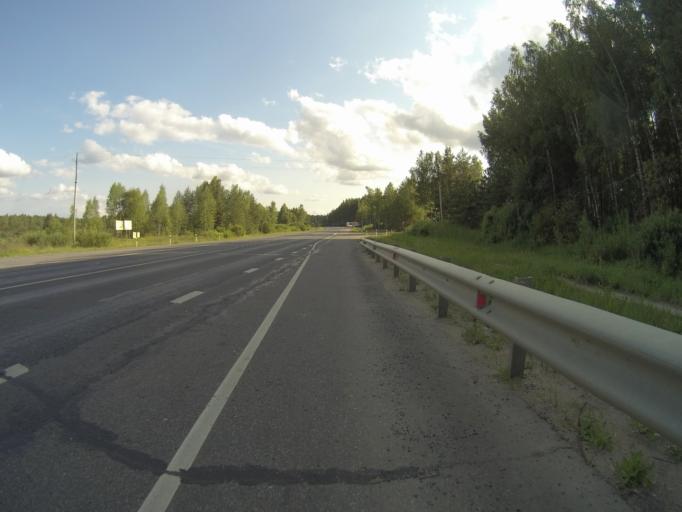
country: RU
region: Ivanovo
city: Nerl'
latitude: 56.6124
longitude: 40.5584
